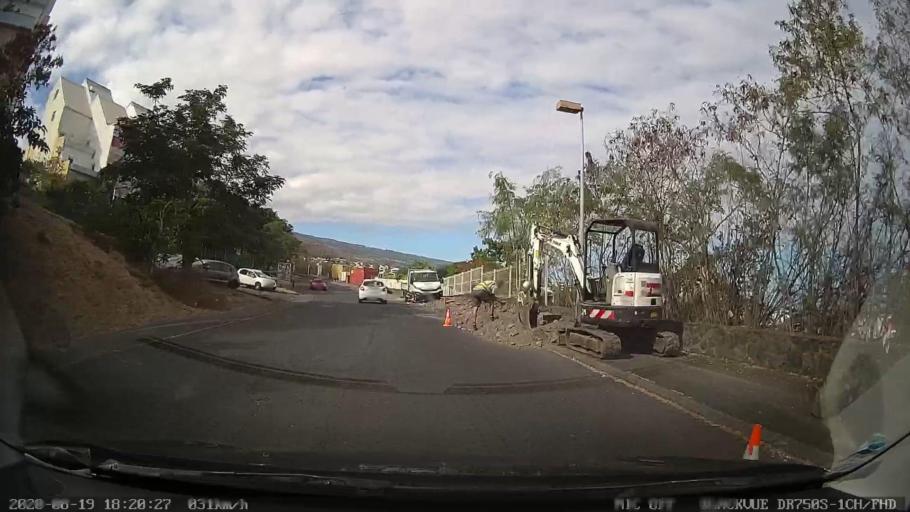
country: RE
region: Reunion
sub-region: Reunion
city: La Possession
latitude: -20.9564
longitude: 55.3320
